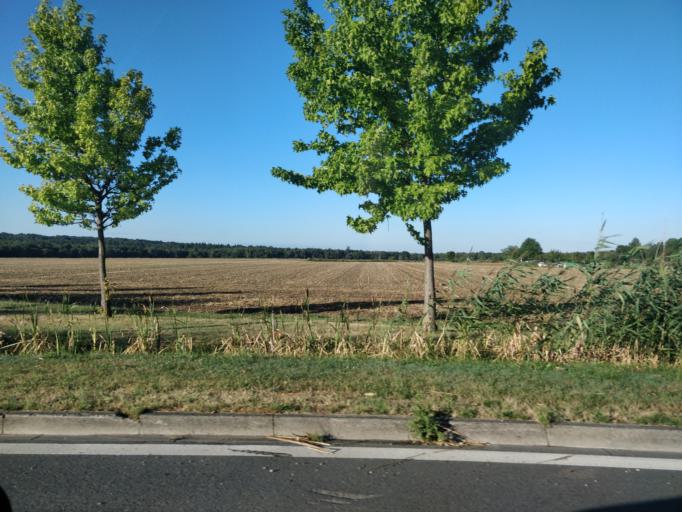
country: FR
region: Picardie
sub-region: Departement de l'Oise
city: Creil
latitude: 49.2537
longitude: 2.4944
